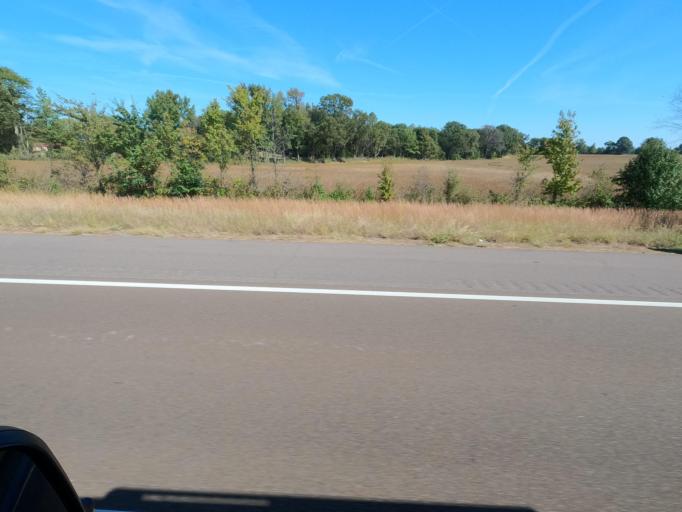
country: US
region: Tennessee
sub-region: Dyer County
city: Dyersburg
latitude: 35.9730
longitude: -89.3375
